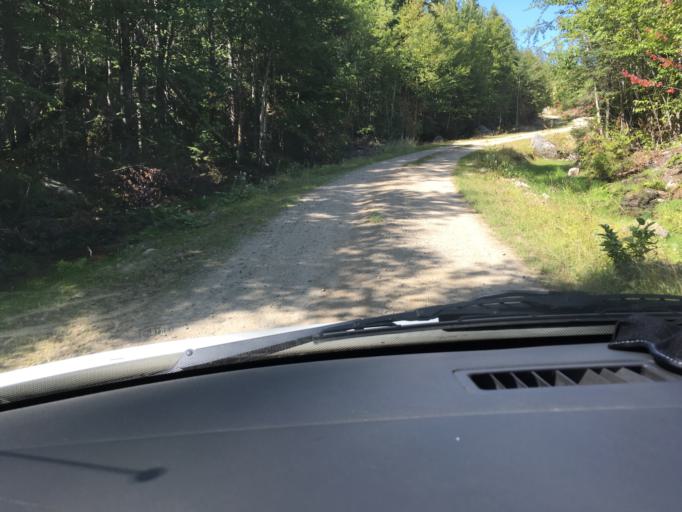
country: US
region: Maine
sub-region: Penobscot County
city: Millinocket
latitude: 45.8454
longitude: -68.7260
